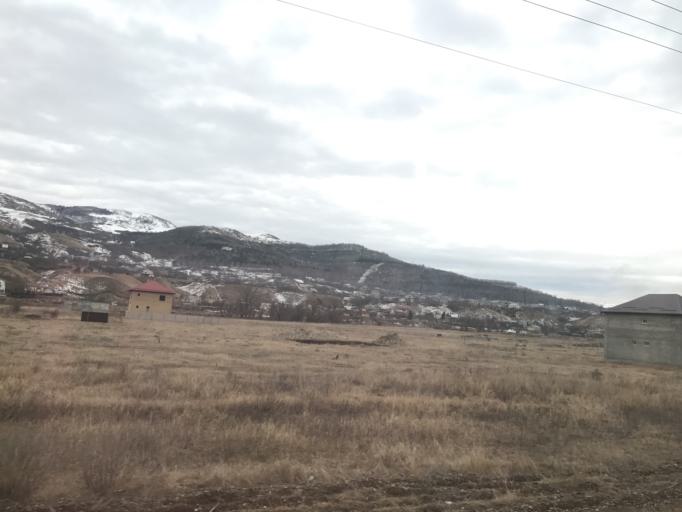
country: RU
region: Stavropol'skiy
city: Kislovodsk
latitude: 43.9493
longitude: 42.7468
